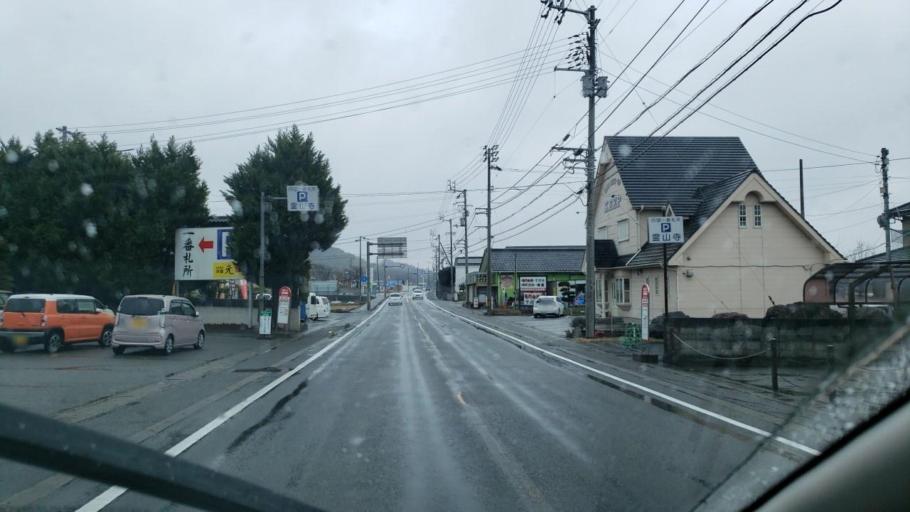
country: JP
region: Tokushima
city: Tokushima-shi
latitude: 34.1589
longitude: 134.5029
